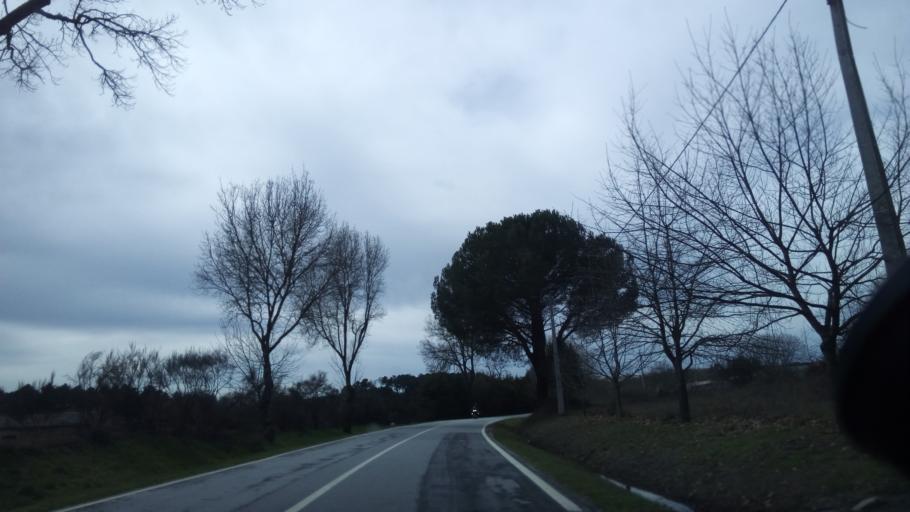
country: PT
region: Guarda
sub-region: Seia
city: Seia
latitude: 40.4544
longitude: -7.7002
